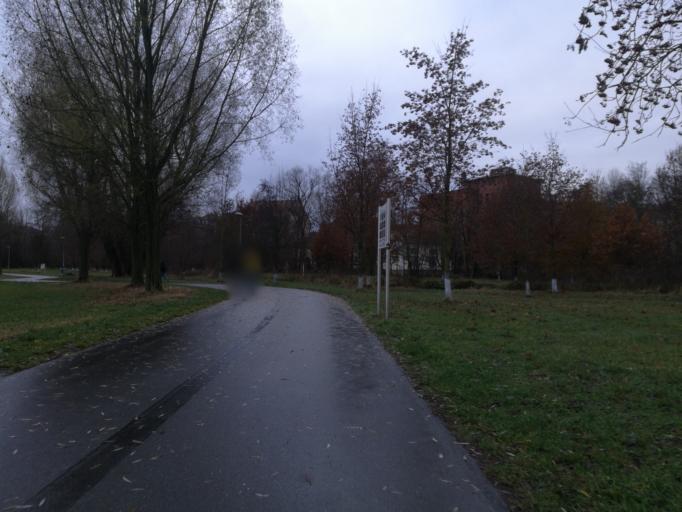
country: DE
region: Bavaria
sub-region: Regierungsbezirk Mittelfranken
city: Furth
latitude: 49.4780
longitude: 10.9939
